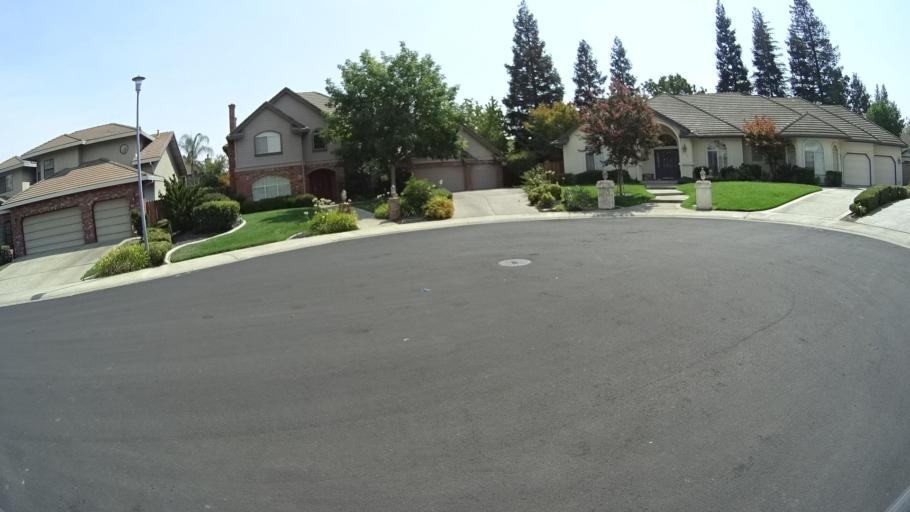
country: US
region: California
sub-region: Sacramento County
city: Elk Grove
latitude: 38.4270
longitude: -121.3795
